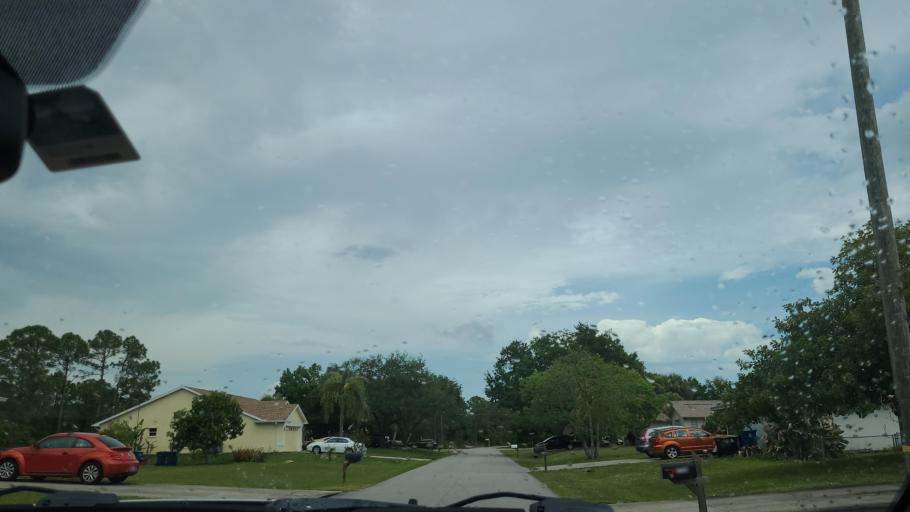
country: US
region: Florida
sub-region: Brevard County
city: Grant-Valkaria
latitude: 27.9464
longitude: -80.6379
